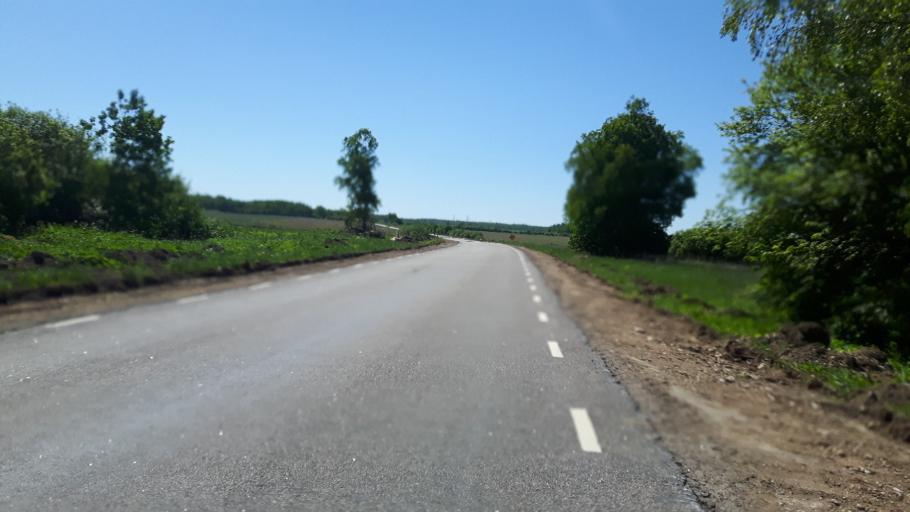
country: EE
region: Ida-Virumaa
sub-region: Narva-Joesuu linn
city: Narva-Joesuu
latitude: 59.3885
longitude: 27.9208
